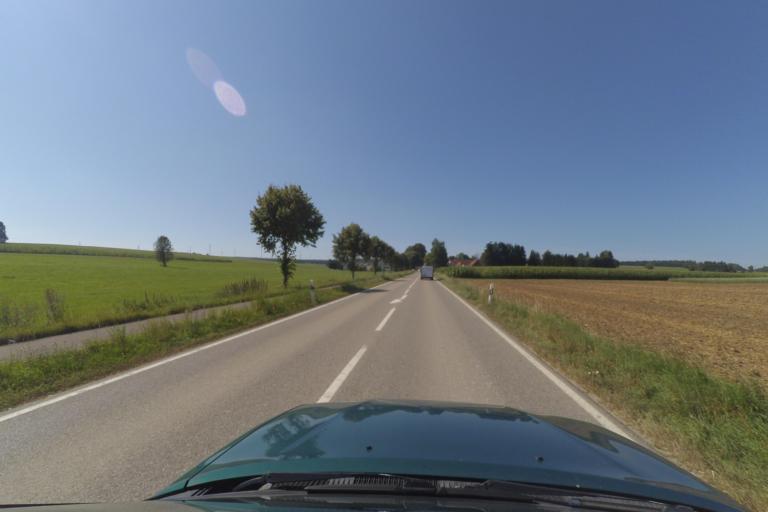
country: DE
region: Baden-Wuerttemberg
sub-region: Regierungsbezirk Stuttgart
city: Bartholoma
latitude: 48.7521
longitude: 9.9749
